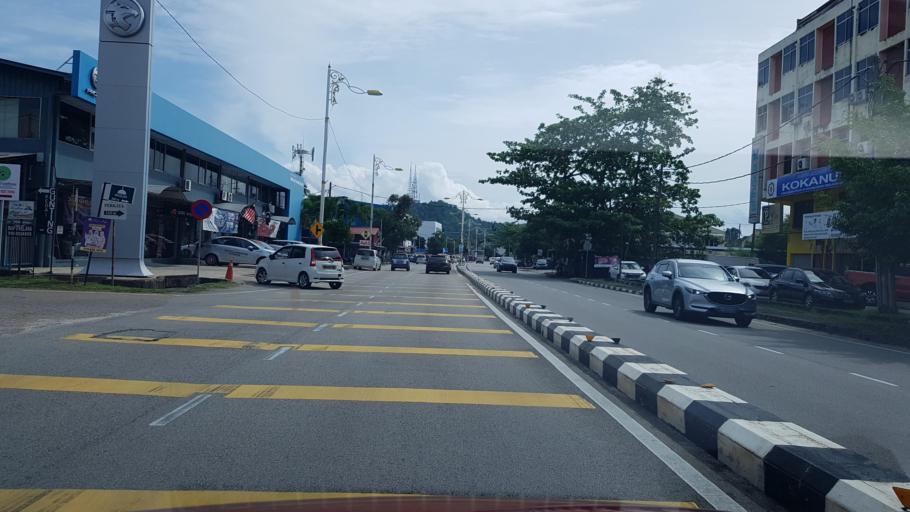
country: MY
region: Terengganu
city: Kuala Terengganu
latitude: 5.3164
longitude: 103.1511
